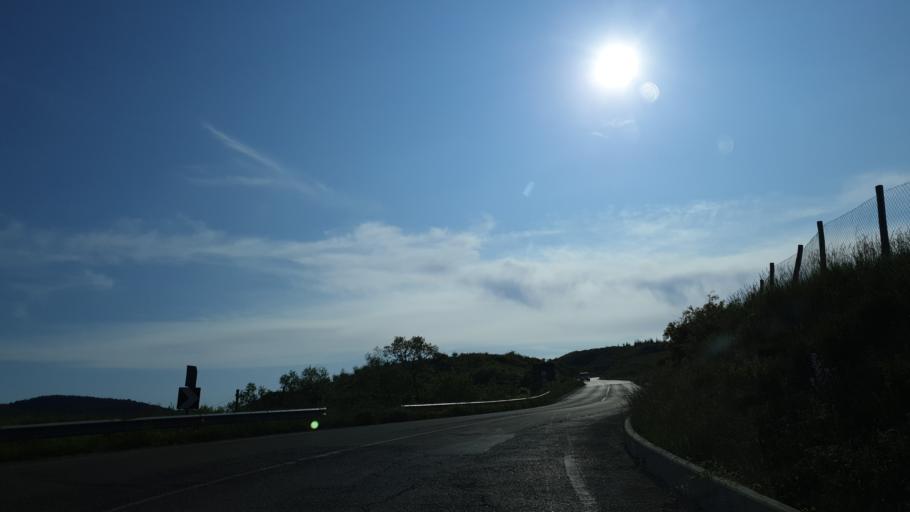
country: IT
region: Tuscany
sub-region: Province of Arezzo
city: Montemignaio
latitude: 43.7844
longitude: 11.6191
